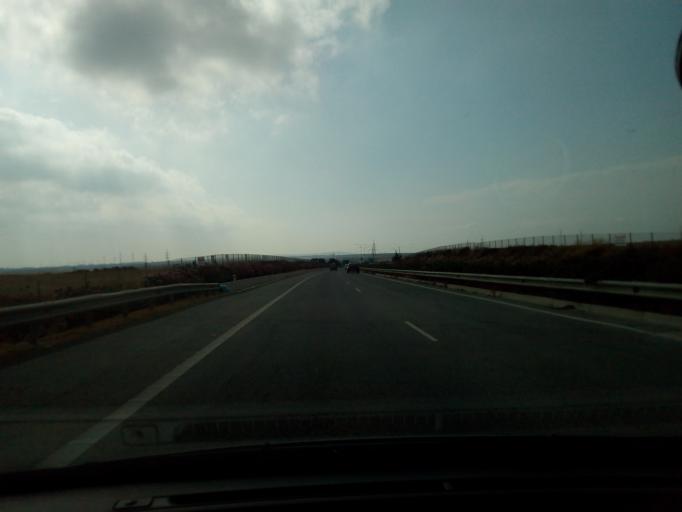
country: CY
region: Larnaka
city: Xylotymbou
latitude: 35.0037
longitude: 33.7495
